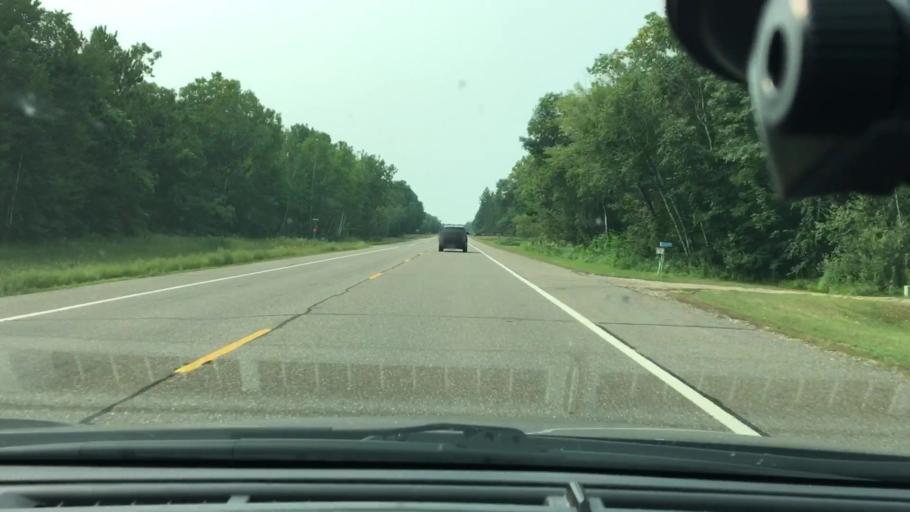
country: US
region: Minnesota
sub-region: Crow Wing County
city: Breezy Point
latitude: 46.5073
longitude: -94.1377
